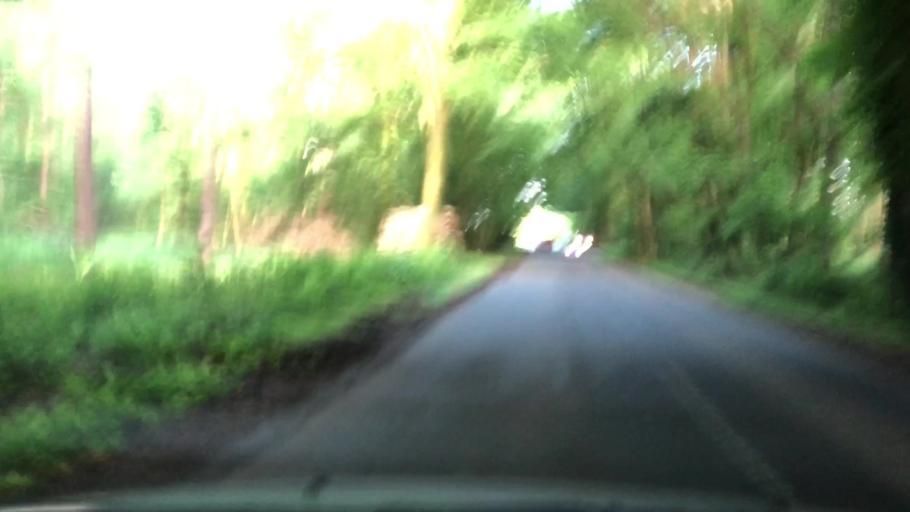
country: GB
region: England
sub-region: Hampshire
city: Alton
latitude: 51.1903
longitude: -1.0131
